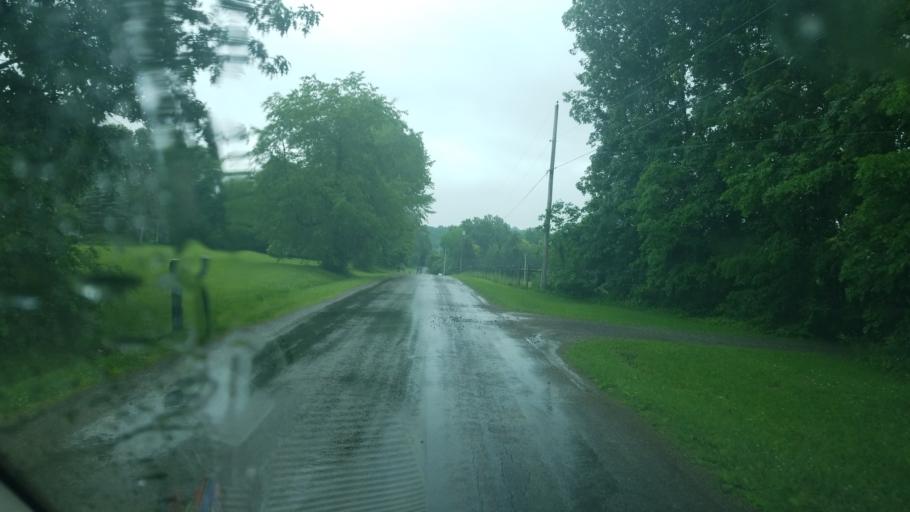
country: US
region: Ohio
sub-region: Sandusky County
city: Bellville
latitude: 40.6236
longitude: -82.4388
